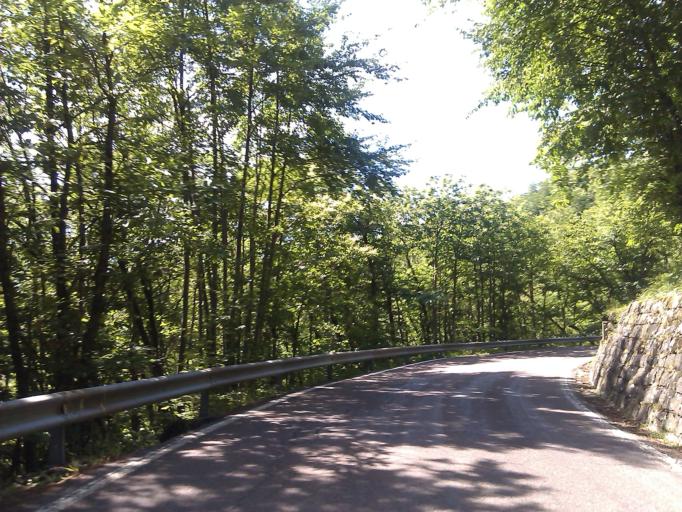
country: IT
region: Tuscany
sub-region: Provincia di Pistoia
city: Sambuca Pistoiese
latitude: 44.1044
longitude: 11.0419
